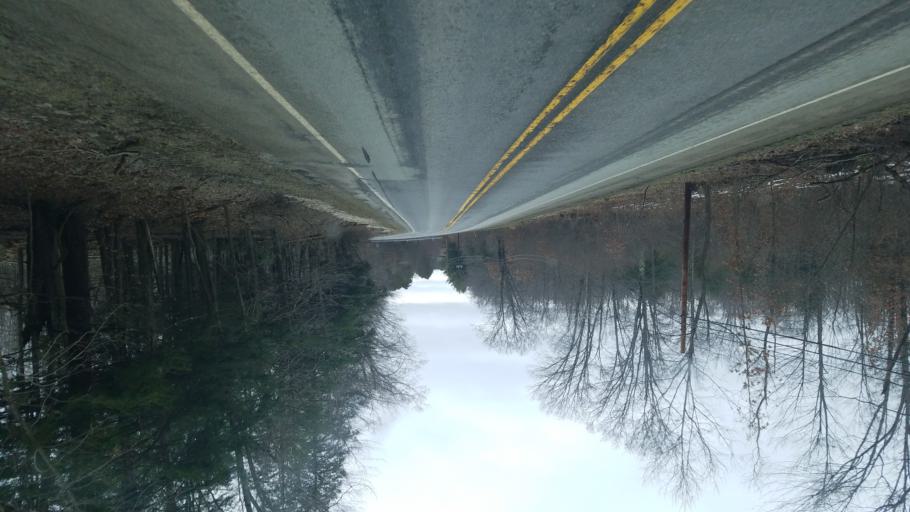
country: US
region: Pennsylvania
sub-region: Forest County
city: Marienville
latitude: 41.4198
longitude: -79.2098
